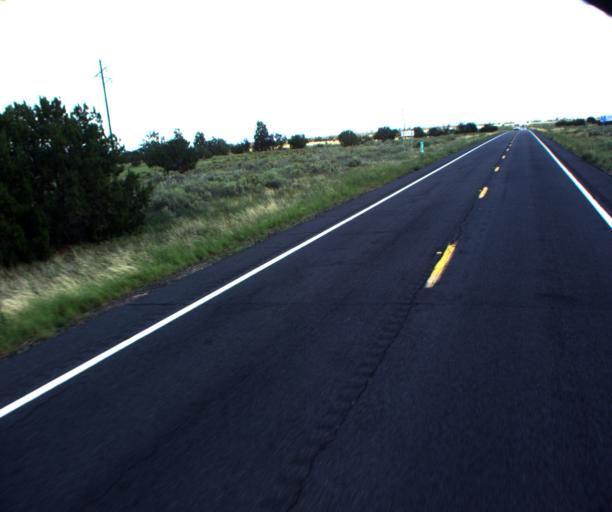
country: US
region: Arizona
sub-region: Coconino County
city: Grand Canyon Village
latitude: 35.6888
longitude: -112.1345
